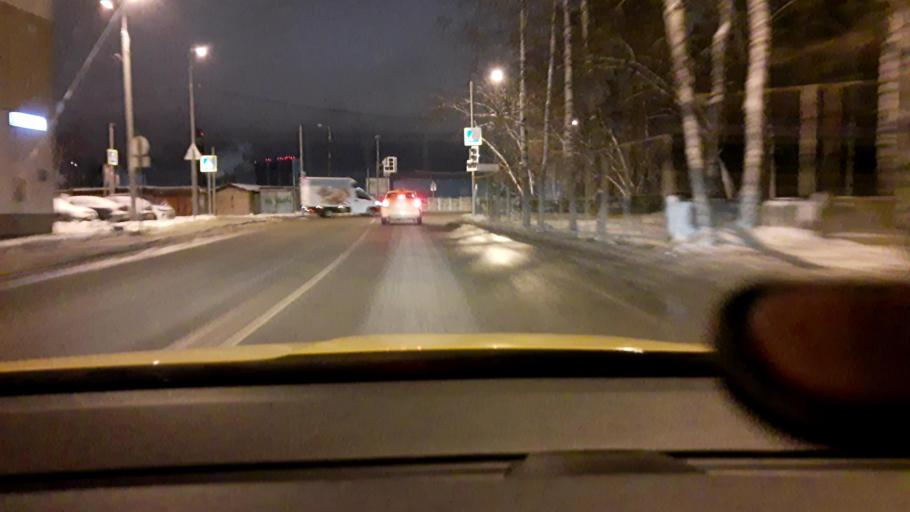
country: RU
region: Moskovskaya
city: Odintsovo
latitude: 55.6698
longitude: 37.2961
